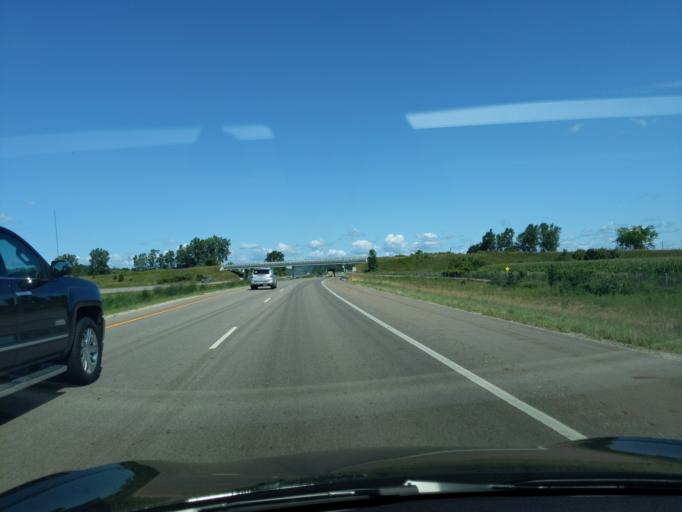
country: US
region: Michigan
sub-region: Gratiot County
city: Ithaca
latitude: 43.3045
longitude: -84.5952
